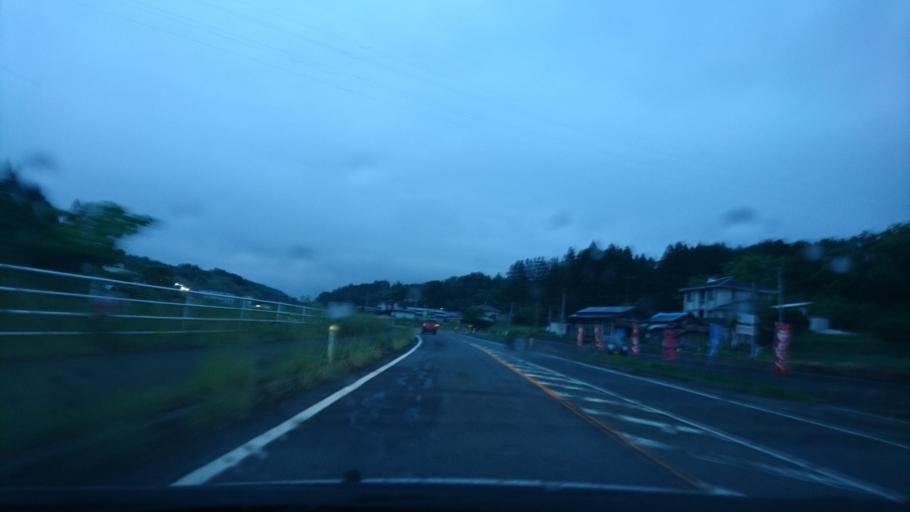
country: JP
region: Iwate
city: Ichinoseki
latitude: 38.7927
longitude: 141.0517
